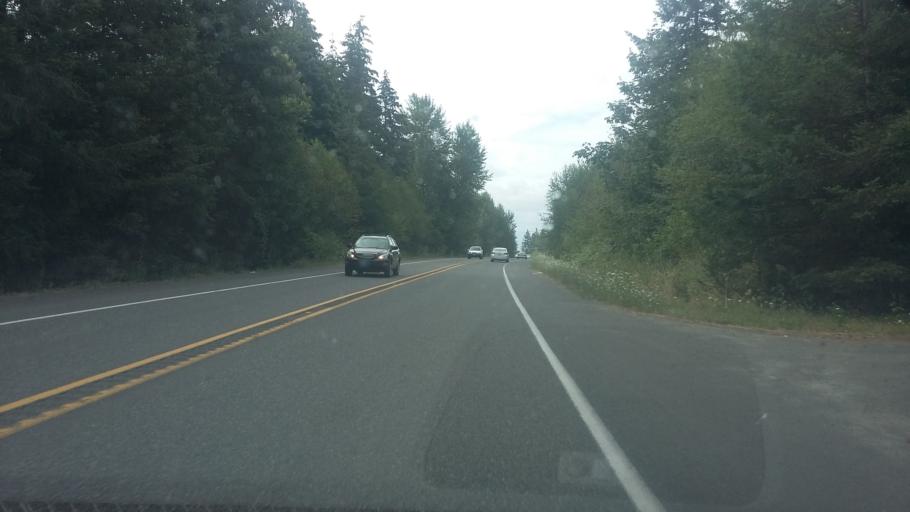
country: US
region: Washington
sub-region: Clark County
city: Battle Ground
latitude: 45.7955
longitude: -122.5476
